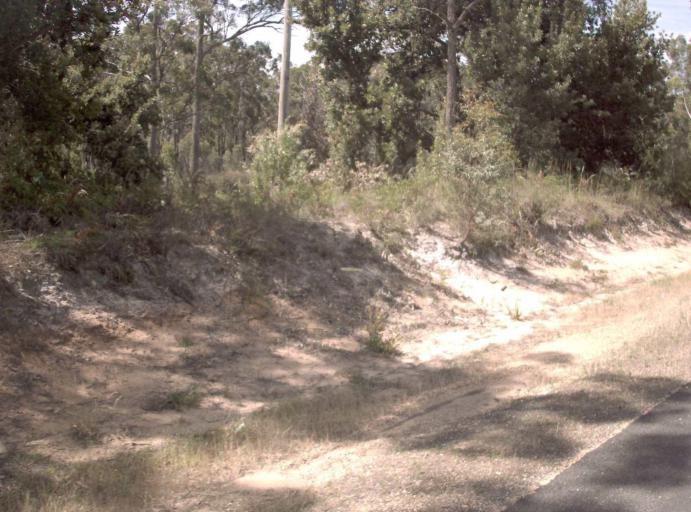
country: AU
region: Victoria
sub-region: Wellington
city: Sale
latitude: -37.9152
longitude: 147.2981
